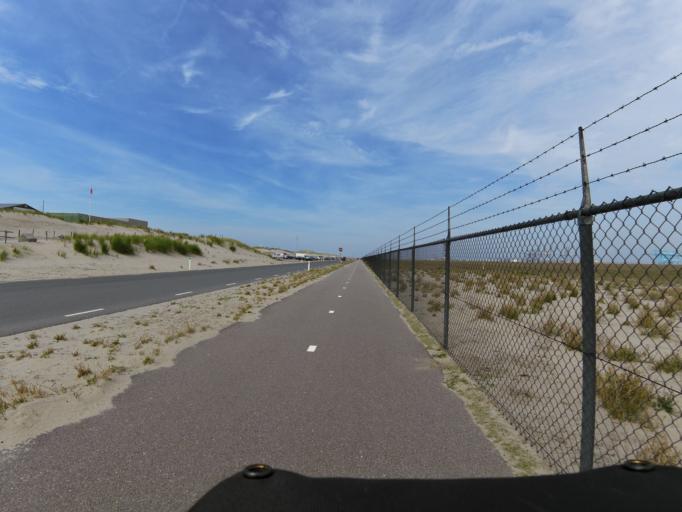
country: NL
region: South Holland
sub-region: Gemeente Goeree-Overflakkee
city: Goedereede
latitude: 51.9264
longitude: 3.9833
